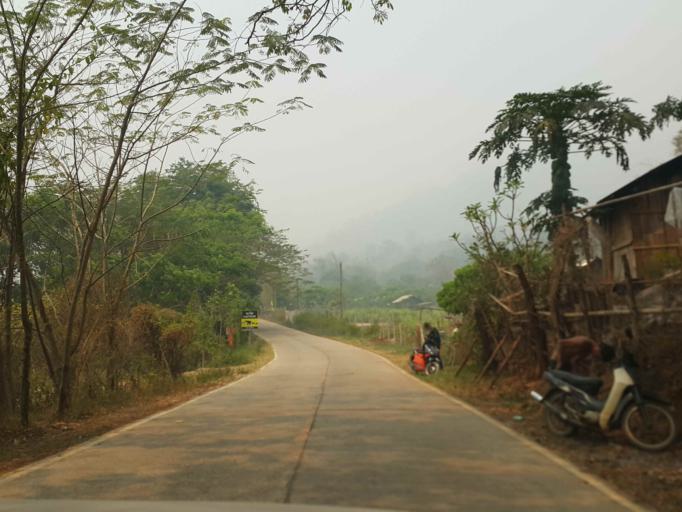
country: TH
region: Chiang Mai
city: Mae Taeng
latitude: 19.2167
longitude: 98.8615
